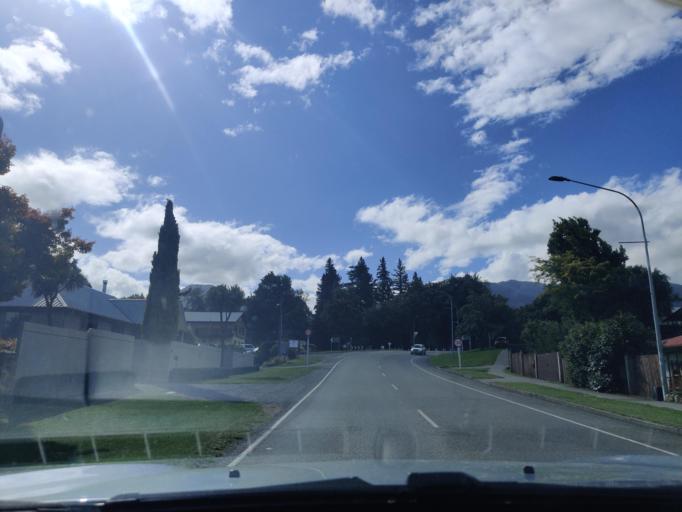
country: NZ
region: Canterbury
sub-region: Hurunui District
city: Amberley
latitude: -42.5266
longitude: 172.8289
